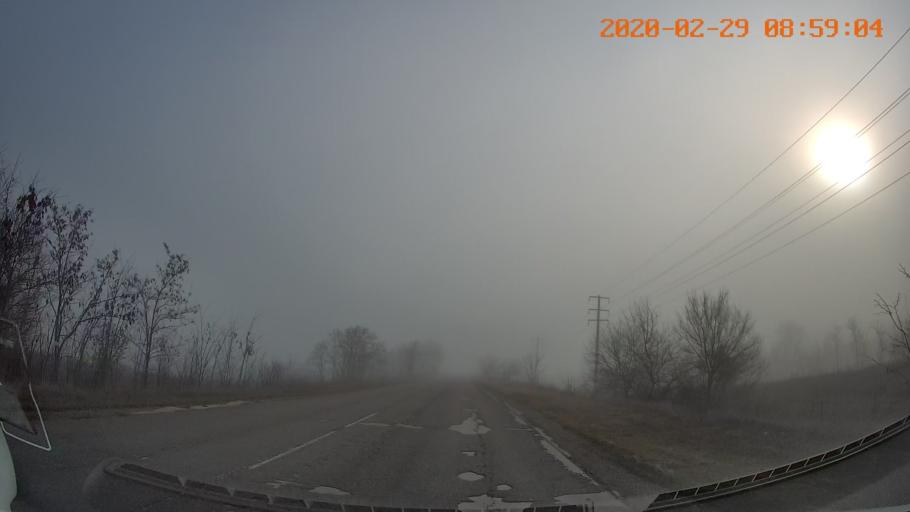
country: MD
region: Telenesti
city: Tiraspolul Nou
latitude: 46.9191
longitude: 29.6517
